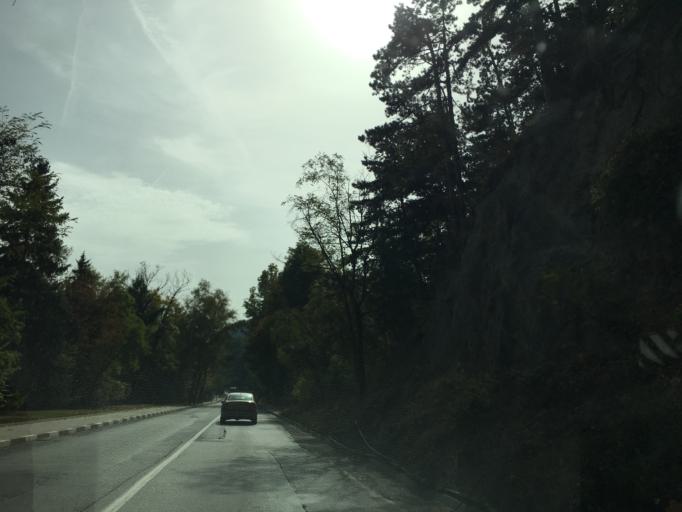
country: BG
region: Sofia-Capital
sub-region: Stolichna Obshtina
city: Sofia
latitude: 42.6020
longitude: 23.4029
